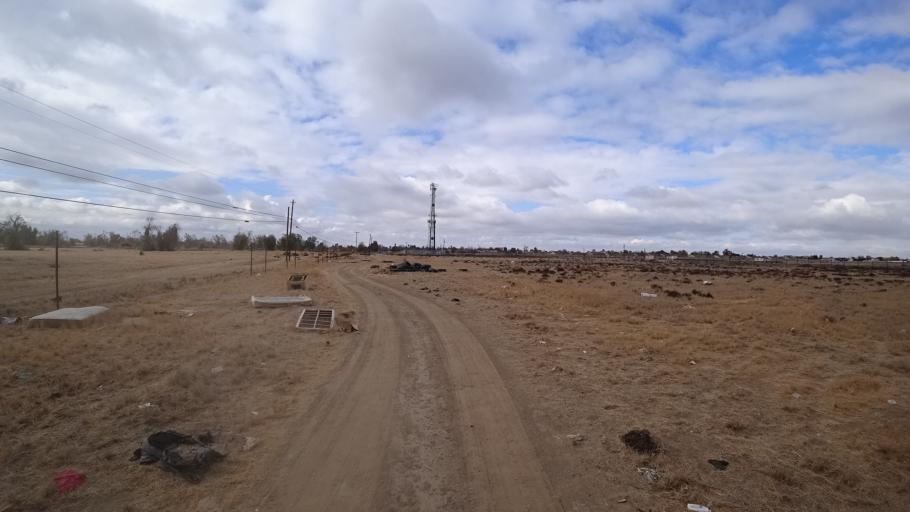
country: US
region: California
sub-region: Kern County
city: Bakersfield
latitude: 35.3395
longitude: -118.9782
